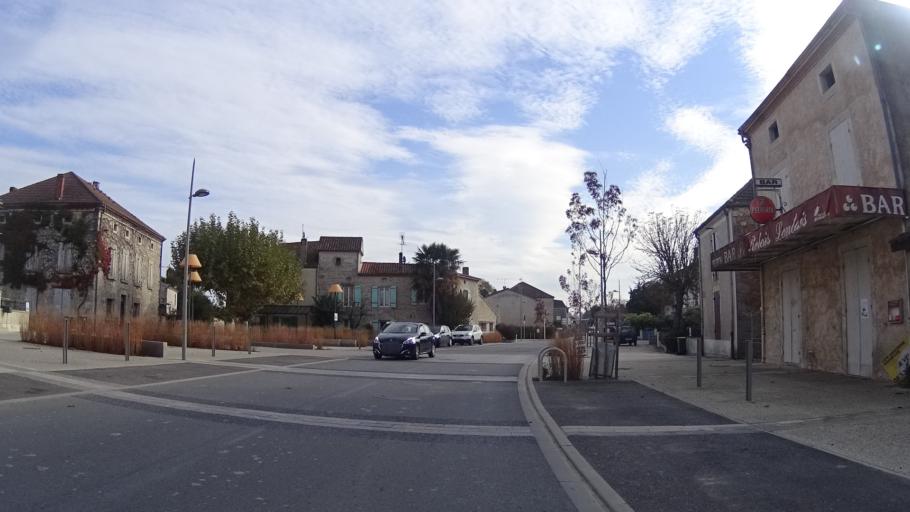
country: FR
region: Aquitaine
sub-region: Departement du Lot-et-Garonne
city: Sainte-Colombe-en-Bruilhois
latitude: 44.2132
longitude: 0.4837
